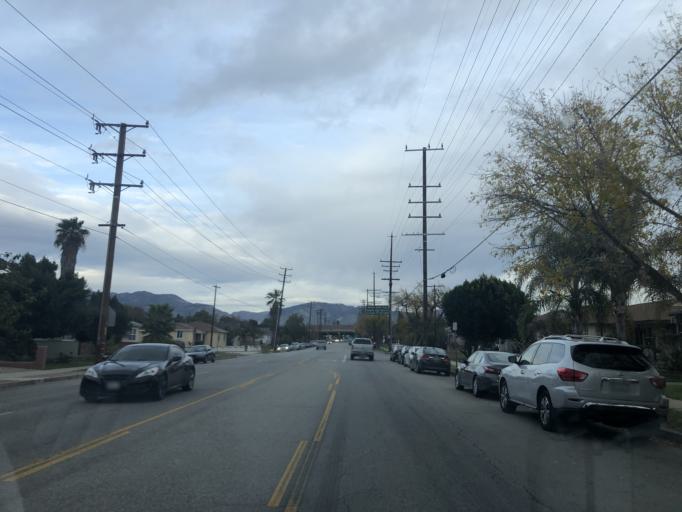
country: US
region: California
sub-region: Los Angeles County
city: San Fernando
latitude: 34.2745
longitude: -118.4561
